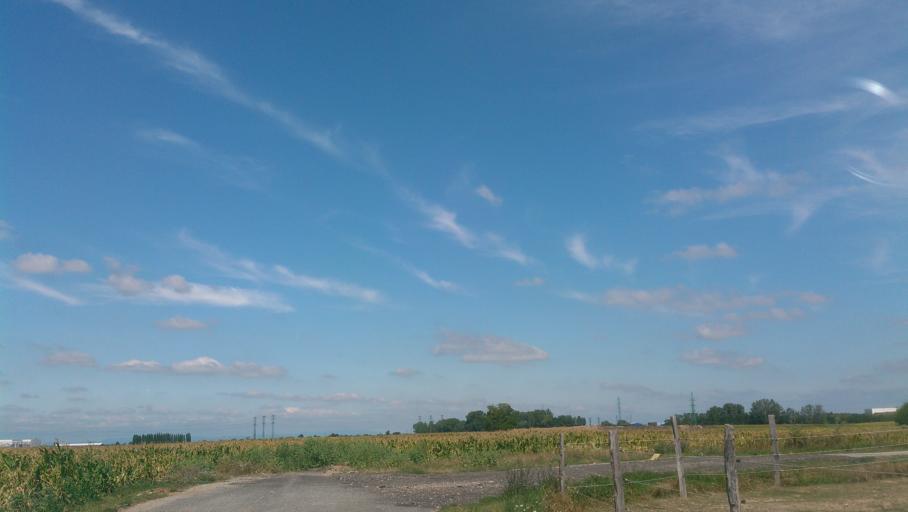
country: SK
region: Nitriansky
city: Sellye
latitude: 48.1742
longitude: 17.8315
